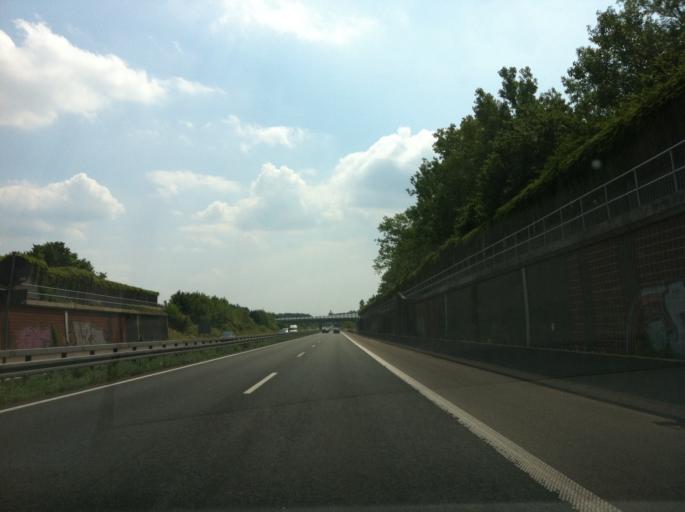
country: DE
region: Hesse
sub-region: Regierungsbezirk Darmstadt
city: Rodgau
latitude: 50.0498
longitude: 8.8905
